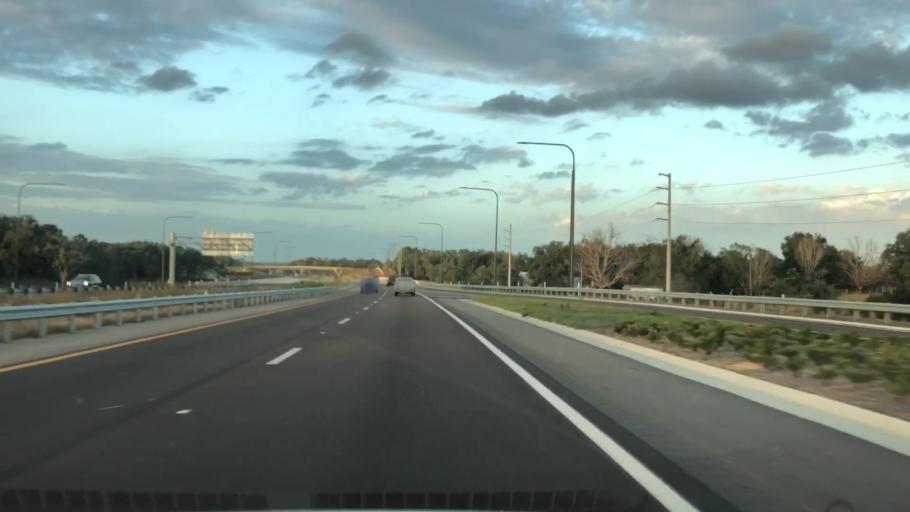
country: US
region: Florida
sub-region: Orange County
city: Zellwood
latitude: 28.7013
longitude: -81.5590
